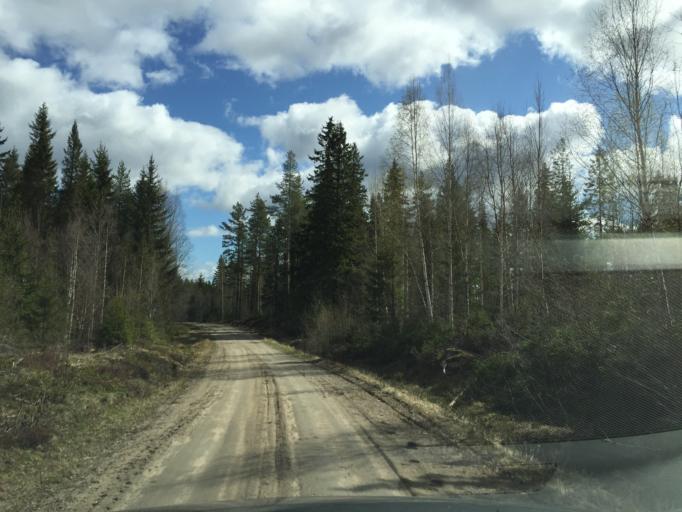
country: SE
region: Gaevleborg
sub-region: Bollnas Kommun
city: Arbra
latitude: 61.5212
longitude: 16.2926
